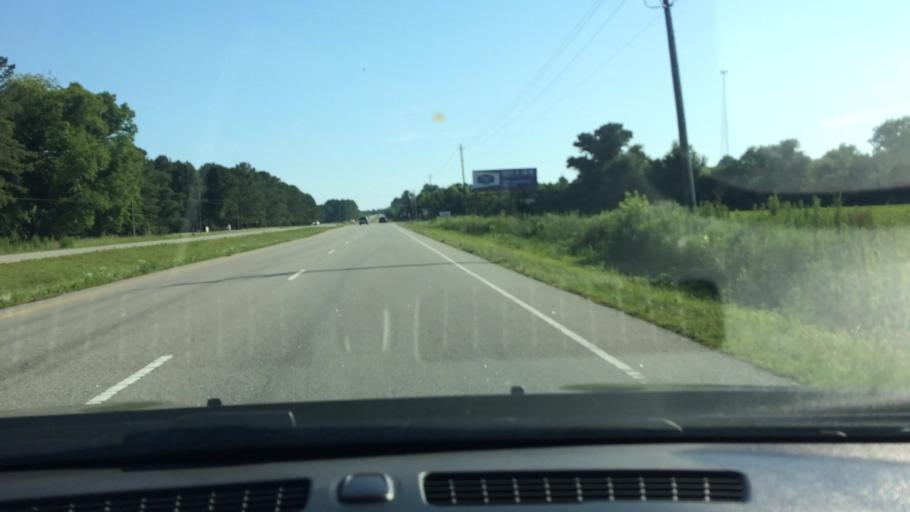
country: US
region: North Carolina
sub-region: Pitt County
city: Grifton
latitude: 35.3401
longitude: -77.4790
